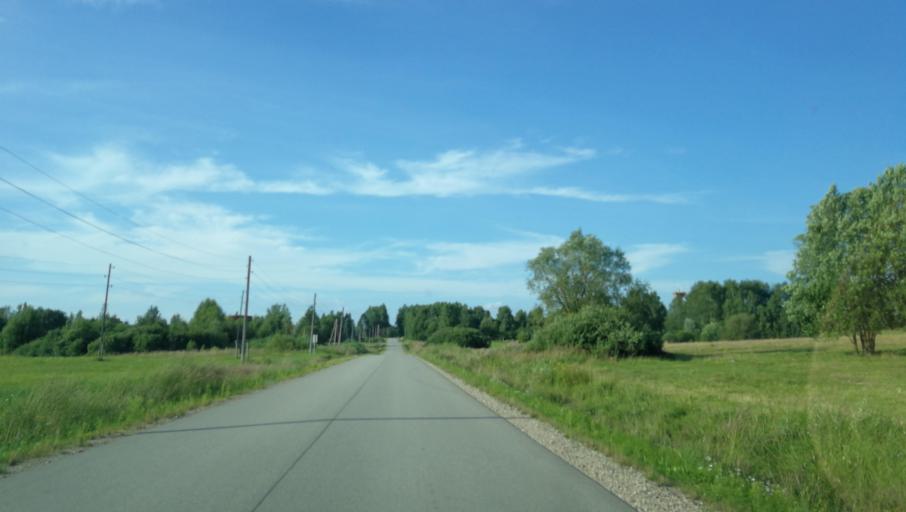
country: LV
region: Pargaujas
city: Stalbe
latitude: 57.3338
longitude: 25.1334
